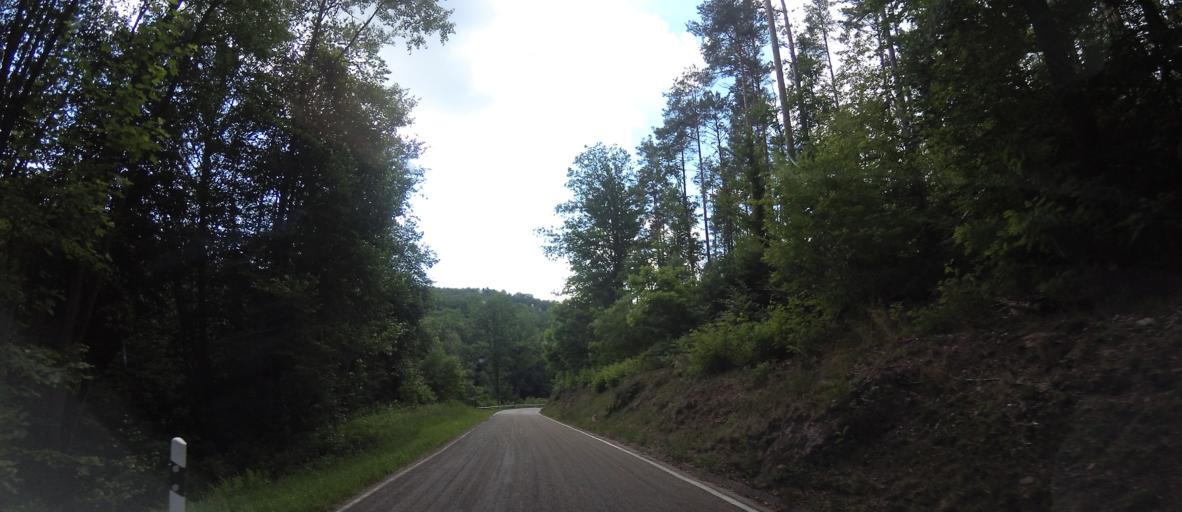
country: DE
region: Rheinland-Pfalz
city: Eppenbrunn
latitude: 49.1087
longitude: 7.5668
